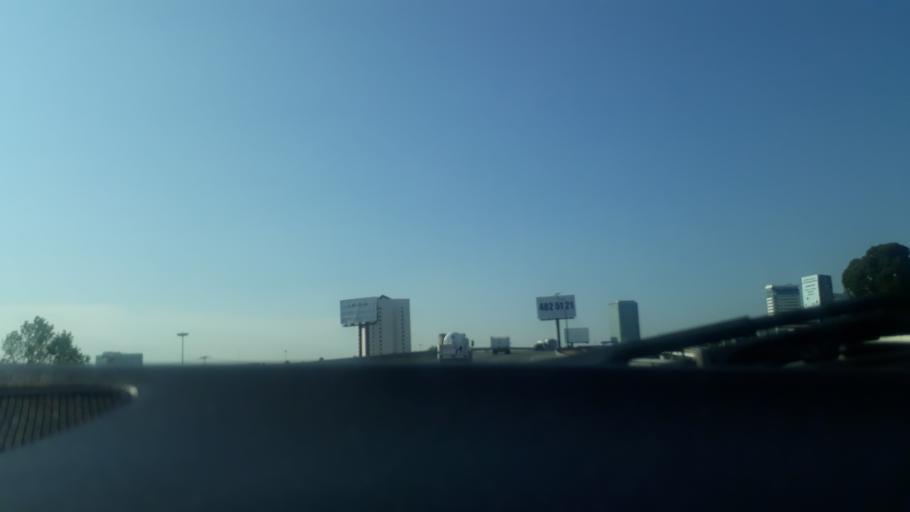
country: MX
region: Puebla
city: Tlazcalancingo
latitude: 19.0113
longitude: -98.2626
